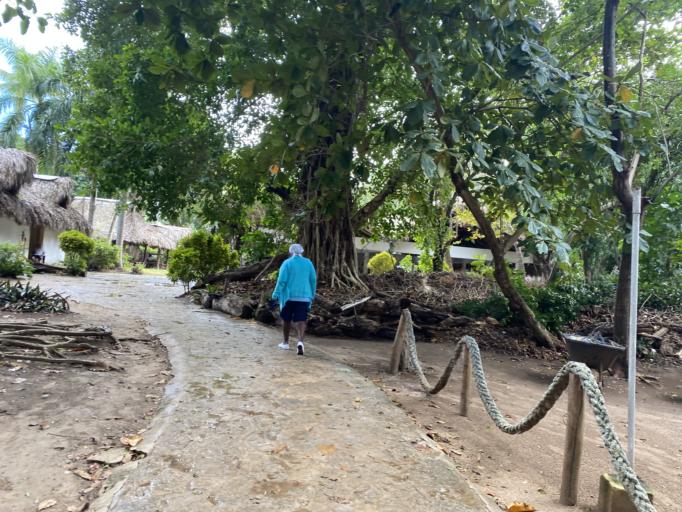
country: DO
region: Samana
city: Samana
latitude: 19.1678
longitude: -69.2782
